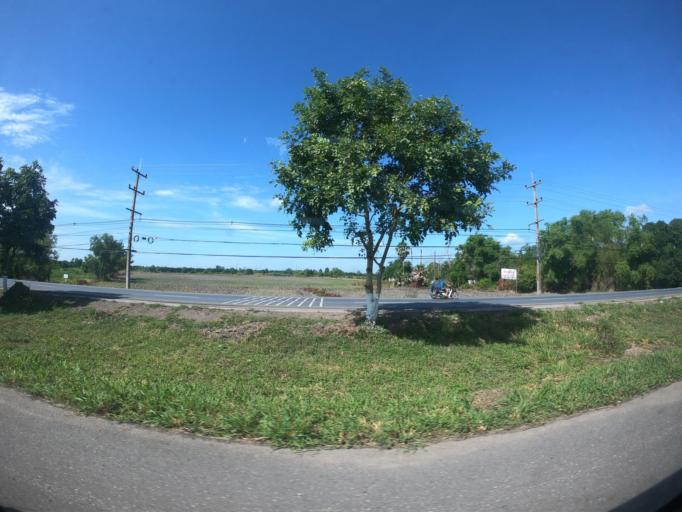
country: TH
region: Nakhon Nayok
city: Nakhon Nayok
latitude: 14.2236
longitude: 101.1822
